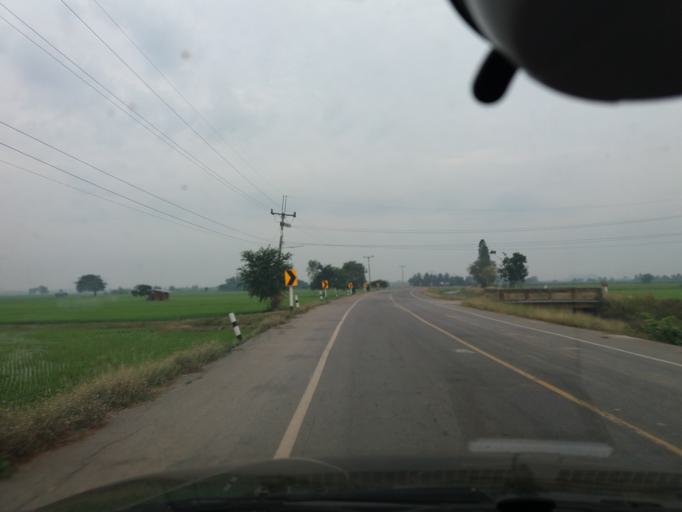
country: TH
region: Suphan Buri
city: Doem Bang Nang Buat
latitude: 14.8747
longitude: 100.1337
